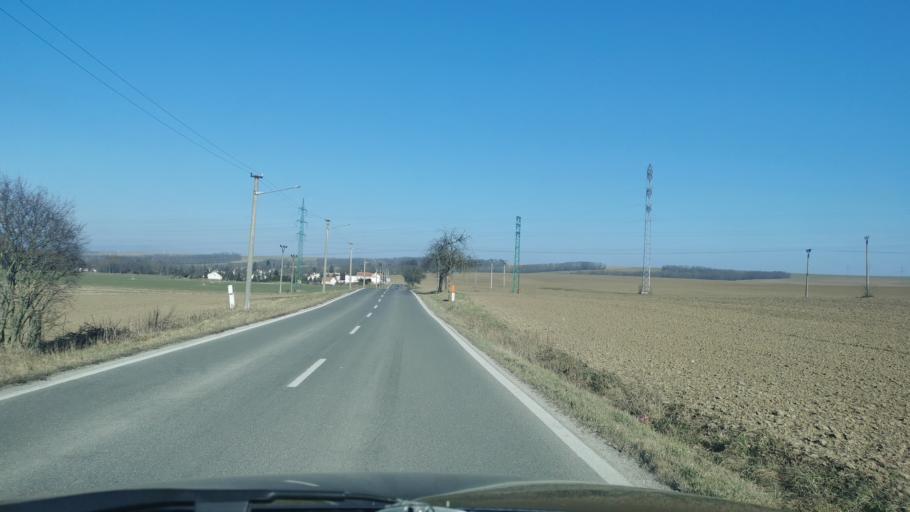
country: SK
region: Trnavsky
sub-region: Okres Senica
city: Senica
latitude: 48.6829
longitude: 17.3913
